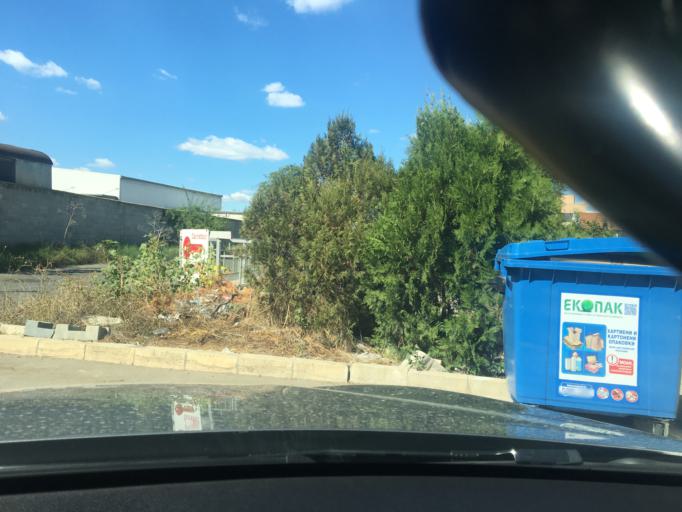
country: BG
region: Burgas
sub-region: Obshtina Burgas
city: Burgas
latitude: 42.5297
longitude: 27.4563
